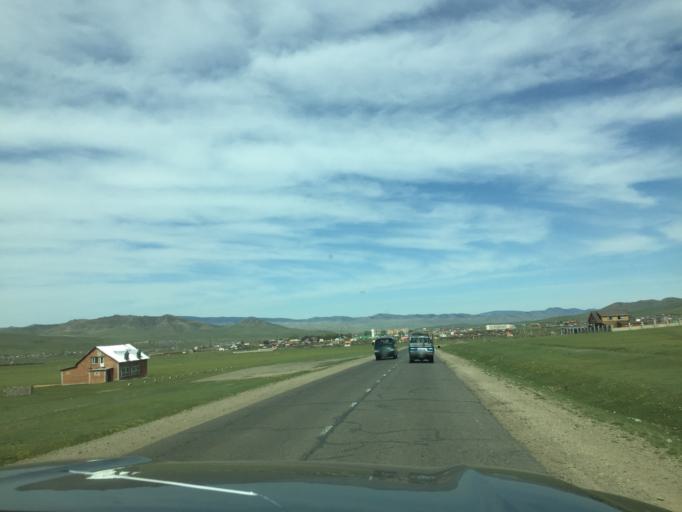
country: MN
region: Central Aimak
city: Ihsueuej
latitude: 48.2158
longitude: 106.3082
